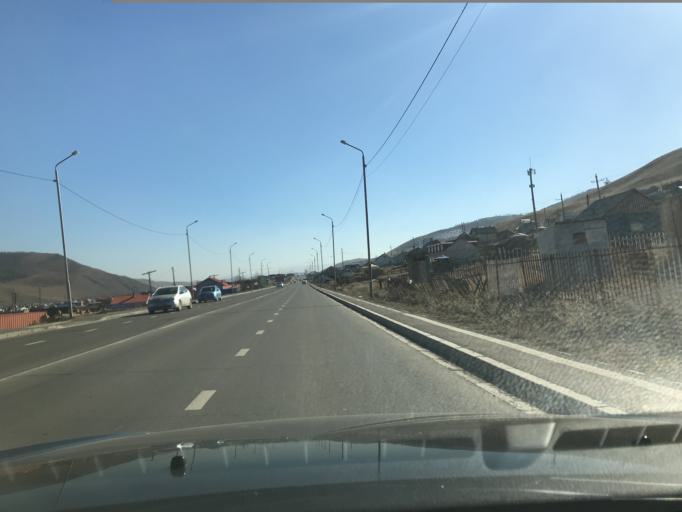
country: MN
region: Ulaanbaatar
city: Ulaanbaatar
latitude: 48.0465
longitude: 106.9014
